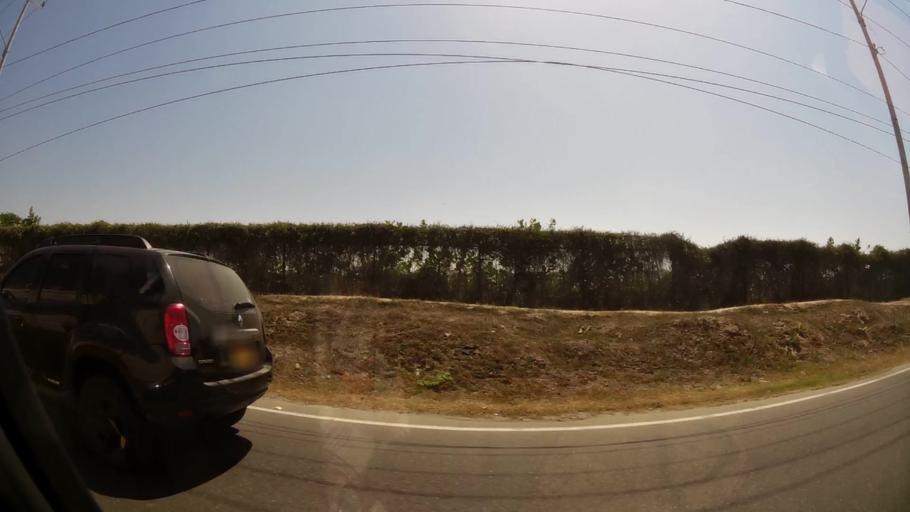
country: CO
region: Bolivar
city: Cartagena
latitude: 10.4401
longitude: -75.5292
